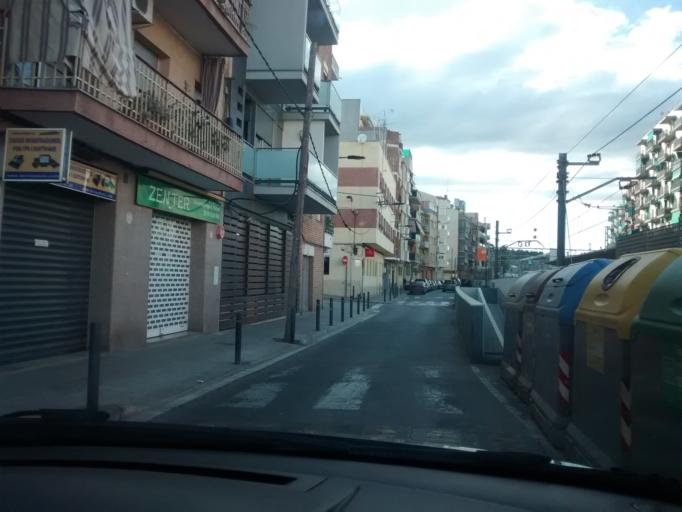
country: ES
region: Catalonia
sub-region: Provincia de Barcelona
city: Sant Vicenc dels Horts
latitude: 41.3989
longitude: 2.0051
